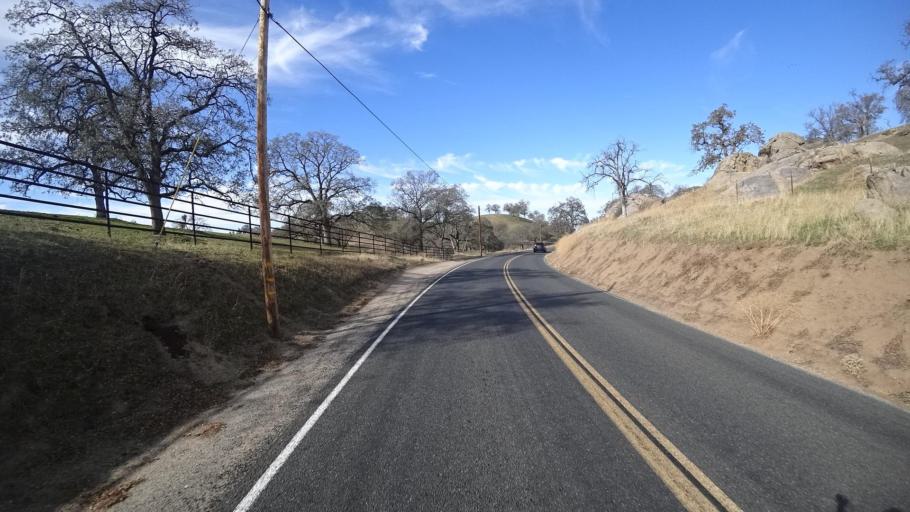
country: US
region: California
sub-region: Kern County
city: Alta Sierra
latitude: 35.6265
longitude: -118.8094
